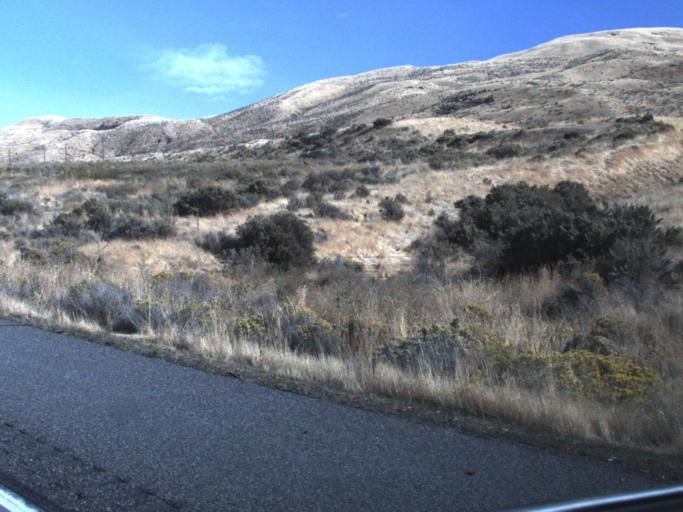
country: US
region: Washington
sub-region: Benton County
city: Benton City
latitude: 46.2586
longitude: -119.5898
